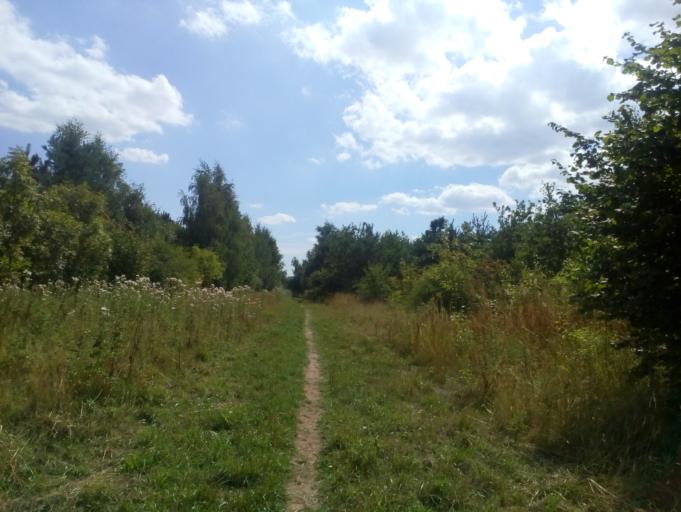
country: GB
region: England
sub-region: North Yorkshire
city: Hambleton
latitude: 53.7651
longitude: -1.1335
